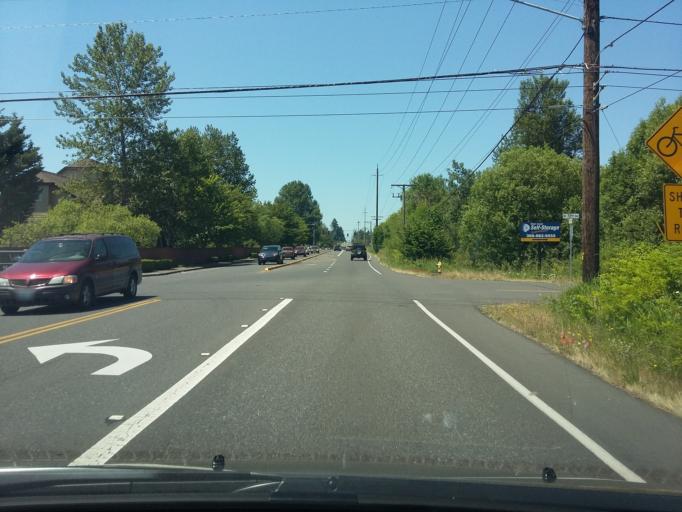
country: US
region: Washington
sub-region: Clark County
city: Walnut Grove
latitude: 45.6789
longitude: -122.5991
